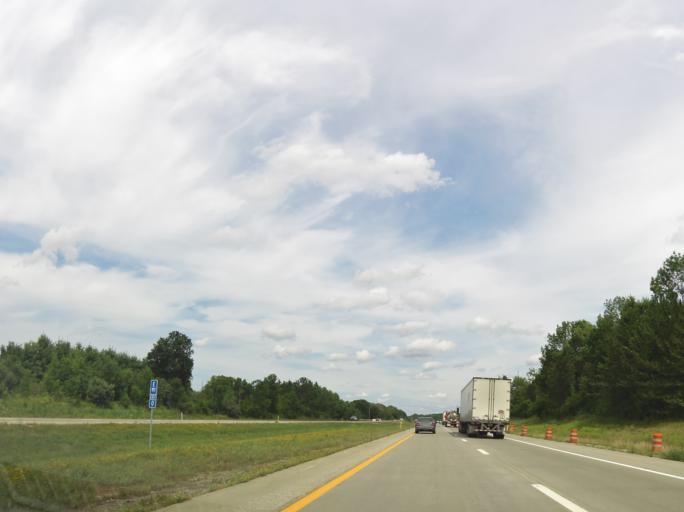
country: US
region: Ohio
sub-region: Lake County
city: Perry
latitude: 41.7183
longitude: -81.1480
